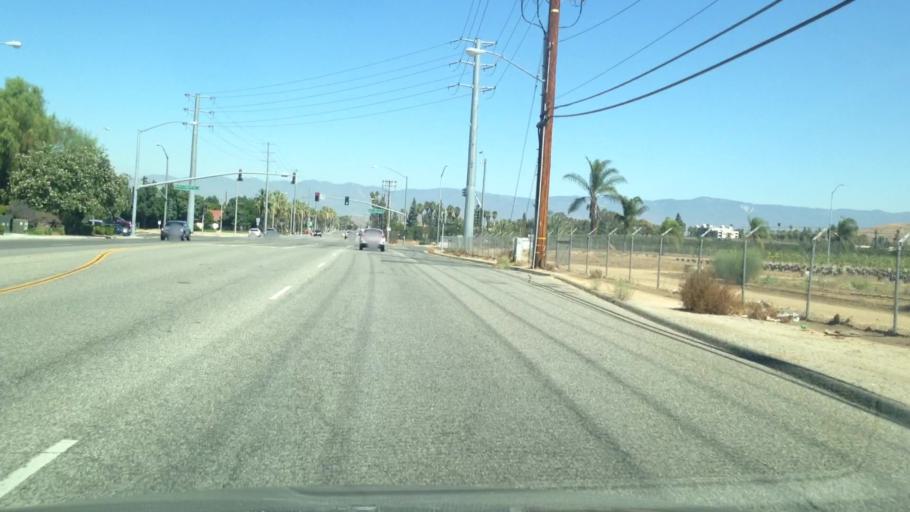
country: US
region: California
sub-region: Riverside County
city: Riverside
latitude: 33.9671
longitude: -117.3485
